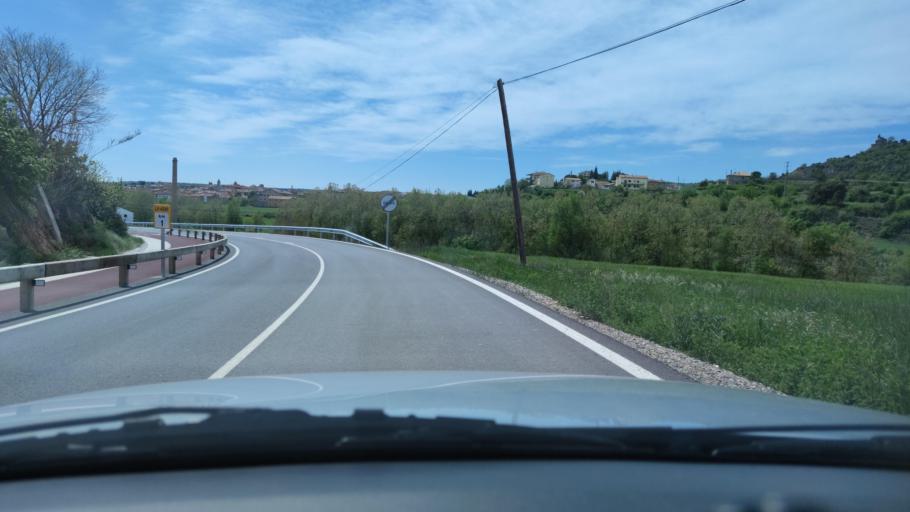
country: ES
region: Catalonia
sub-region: Provincia de Lleida
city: Solsona
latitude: 42.0035
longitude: 1.5167
